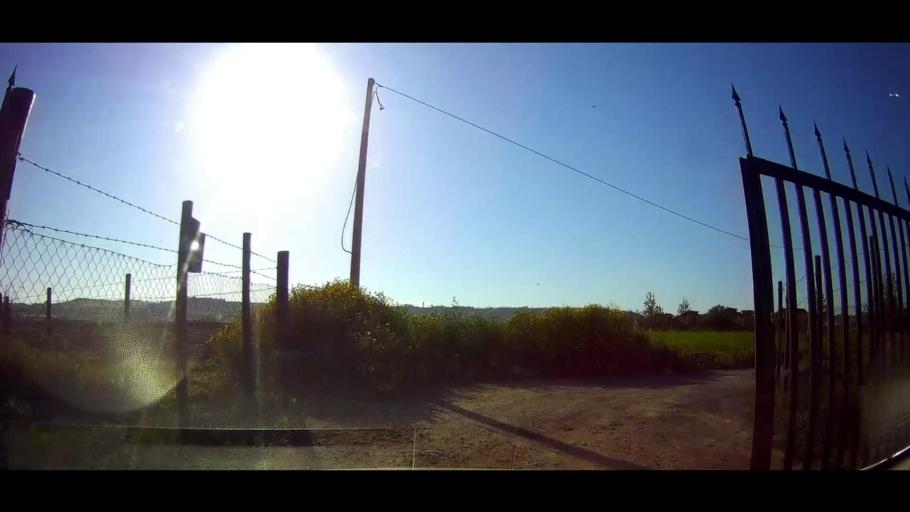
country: IT
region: Calabria
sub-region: Provincia di Crotone
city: Crotone
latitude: 39.0197
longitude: 17.1866
